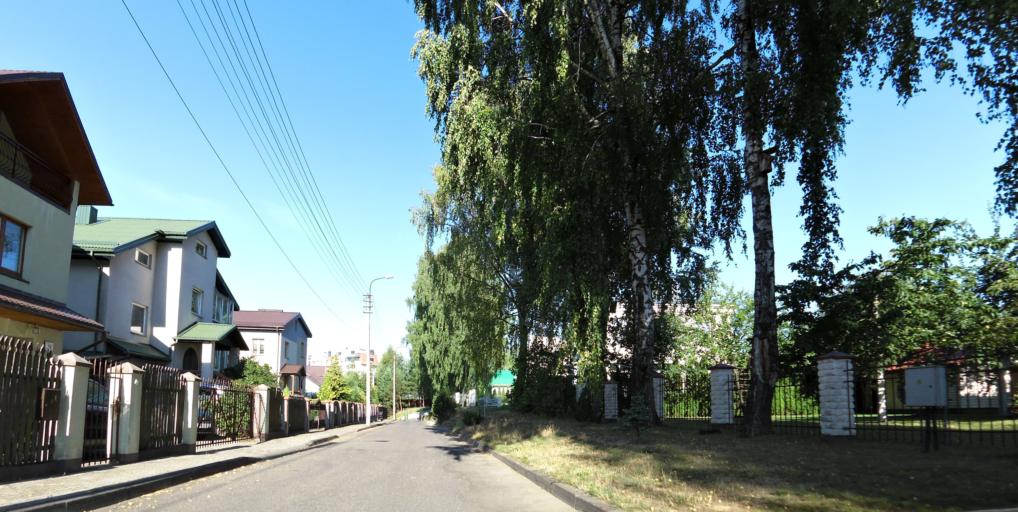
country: LT
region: Vilnius County
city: Pilaite
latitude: 54.7137
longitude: 25.1913
